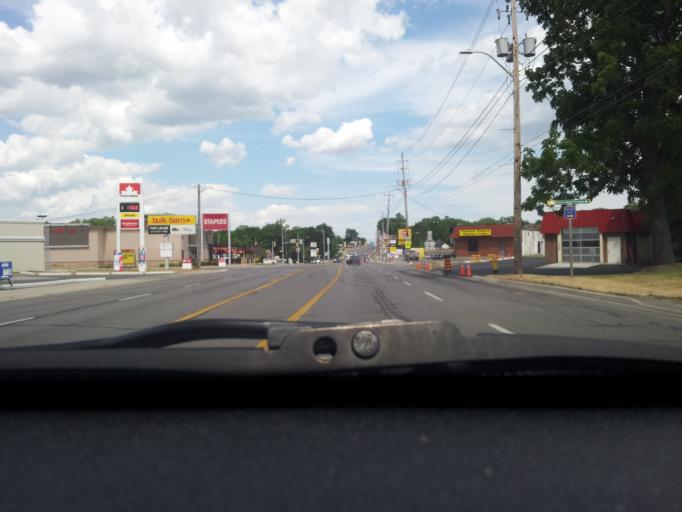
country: CA
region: Ontario
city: Norfolk County
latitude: 42.8458
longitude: -80.3093
